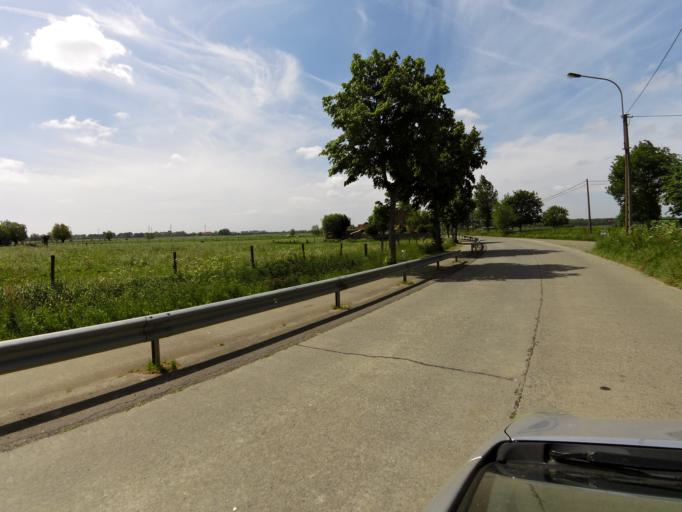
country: BE
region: Flanders
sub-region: Provincie West-Vlaanderen
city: Diksmuide
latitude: 50.9634
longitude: 2.8365
